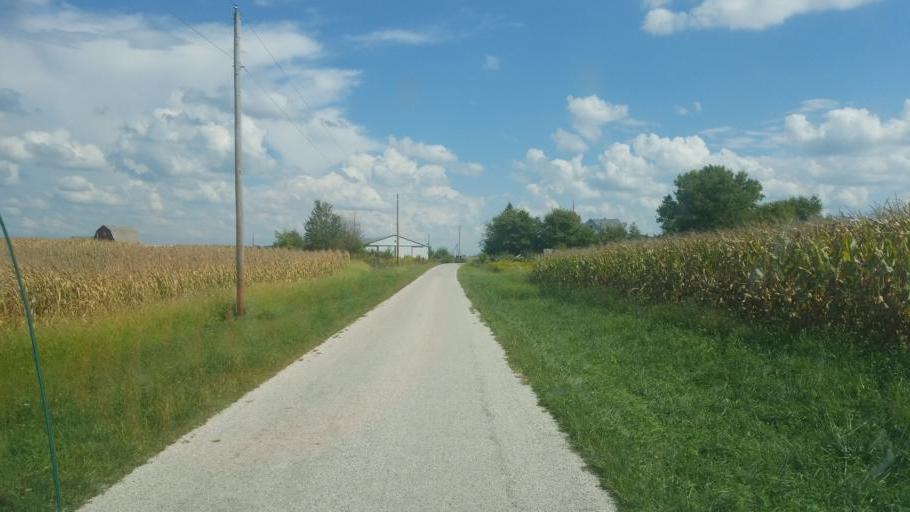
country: US
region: Ohio
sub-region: Seneca County
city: Tiffin
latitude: 40.9736
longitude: -83.2077
